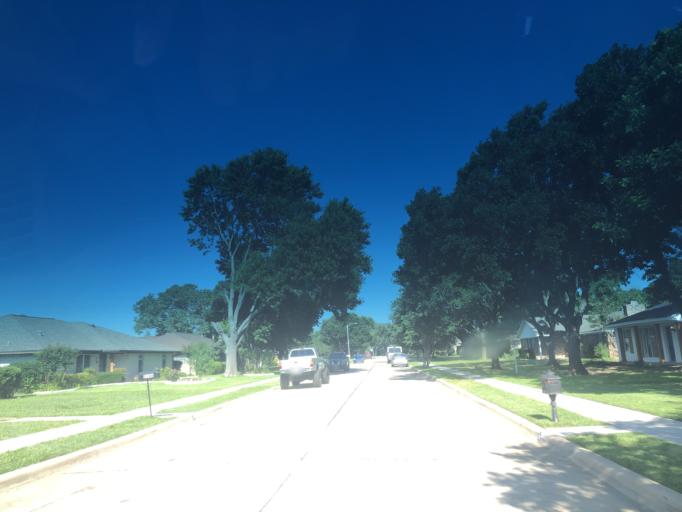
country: US
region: Texas
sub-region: Dallas County
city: Grand Prairie
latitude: 32.7147
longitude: -97.0156
